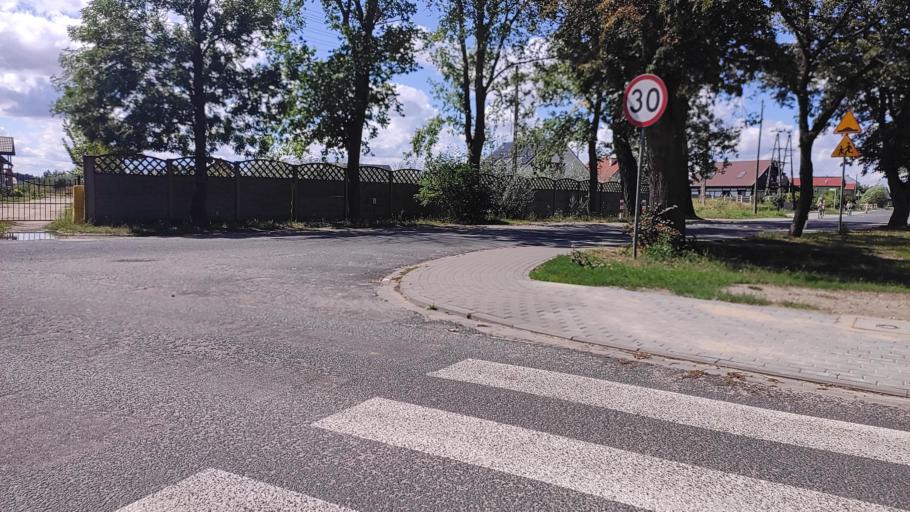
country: PL
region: Greater Poland Voivodeship
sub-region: Powiat poznanski
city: Kleszczewo
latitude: 52.3815
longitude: 17.1620
